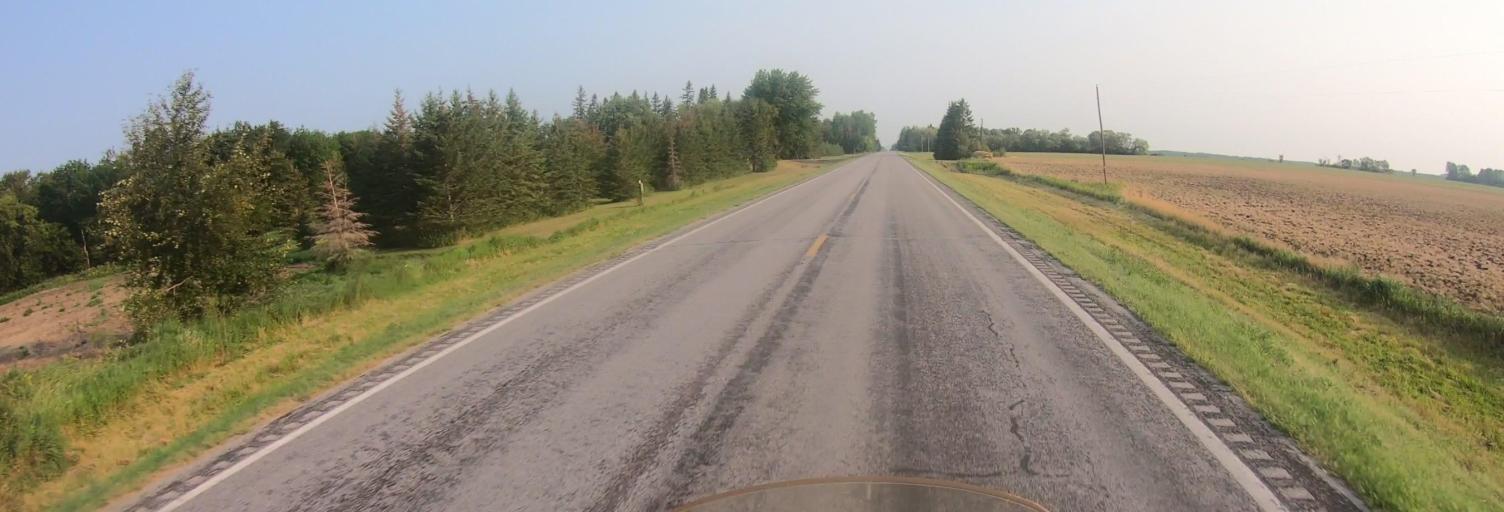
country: US
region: Minnesota
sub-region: Roseau County
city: Warroad
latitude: 48.7762
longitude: -95.3305
